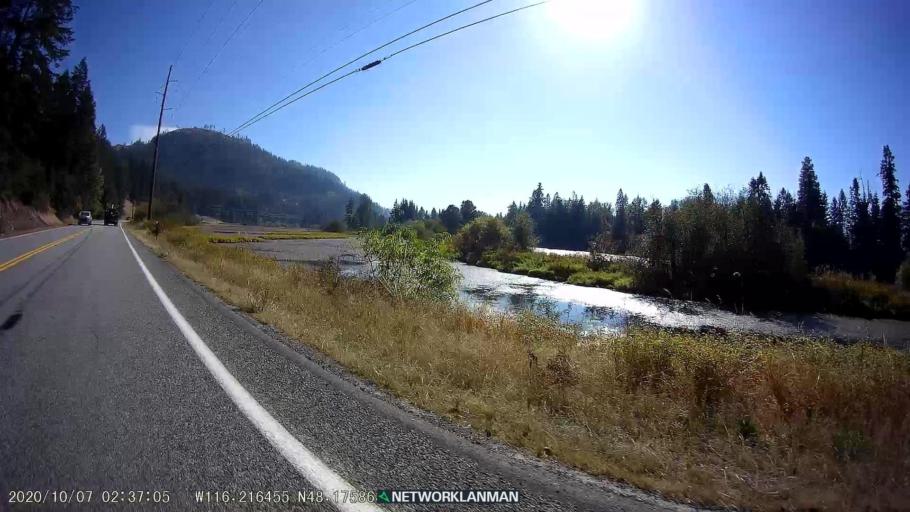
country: US
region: Idaho
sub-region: Bonner County
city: Ponderay
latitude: 48.1759
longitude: -116.2152
